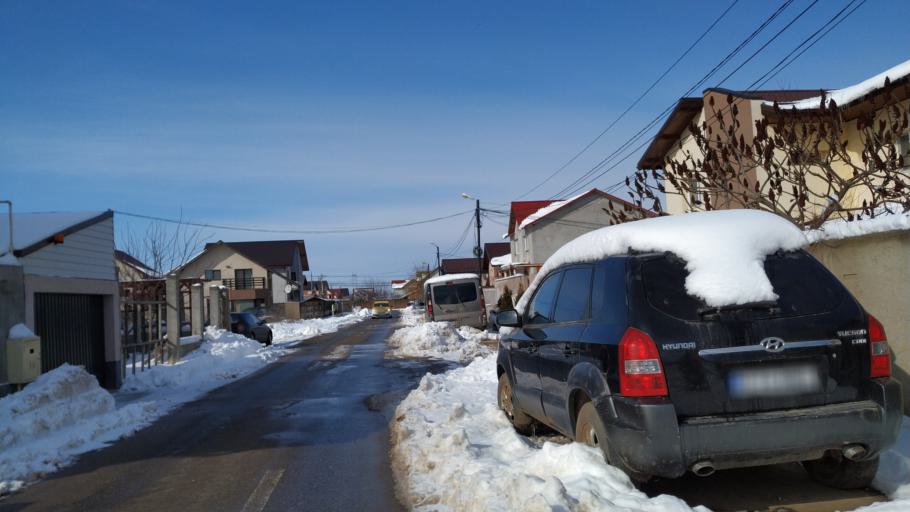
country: RO
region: Ilfov
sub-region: Comuna Berceni
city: Berceni
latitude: 44.3233
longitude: 26.1894
